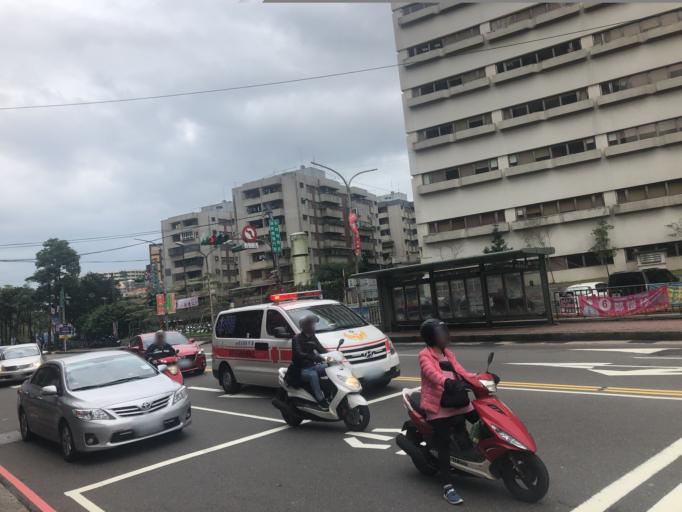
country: TW
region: Taiwan
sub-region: Keelung
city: Keelung
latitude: 25.1209
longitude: 121.7220
